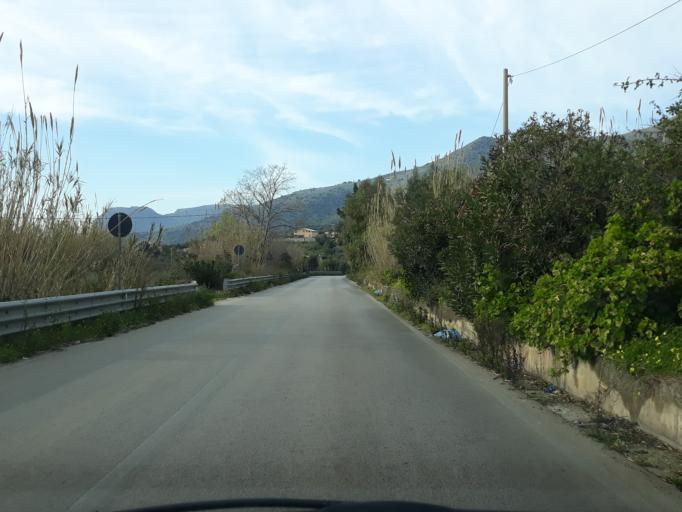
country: IT
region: Sicily
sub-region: Palermo
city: Giardinello
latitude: 38.0722
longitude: 13.1541
